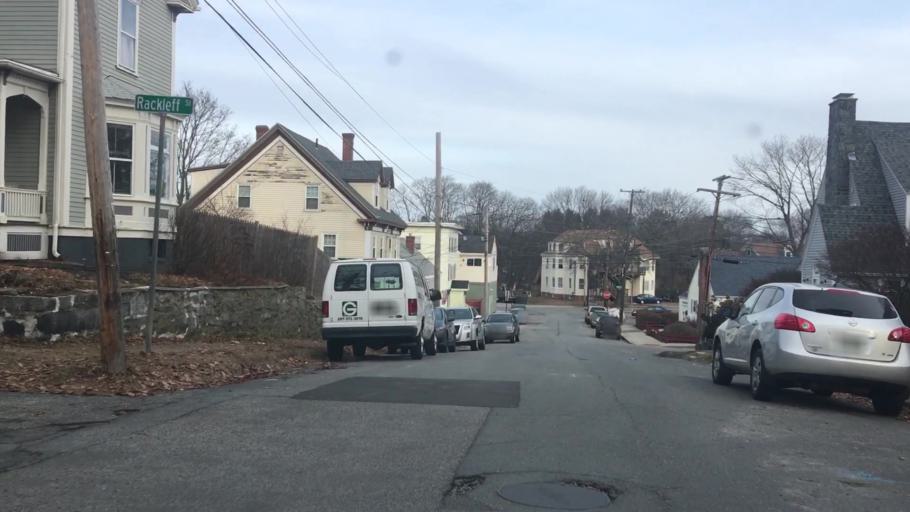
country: US
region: Maine
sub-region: Cumberland County
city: Portland
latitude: 43.6690
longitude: -70.2898
